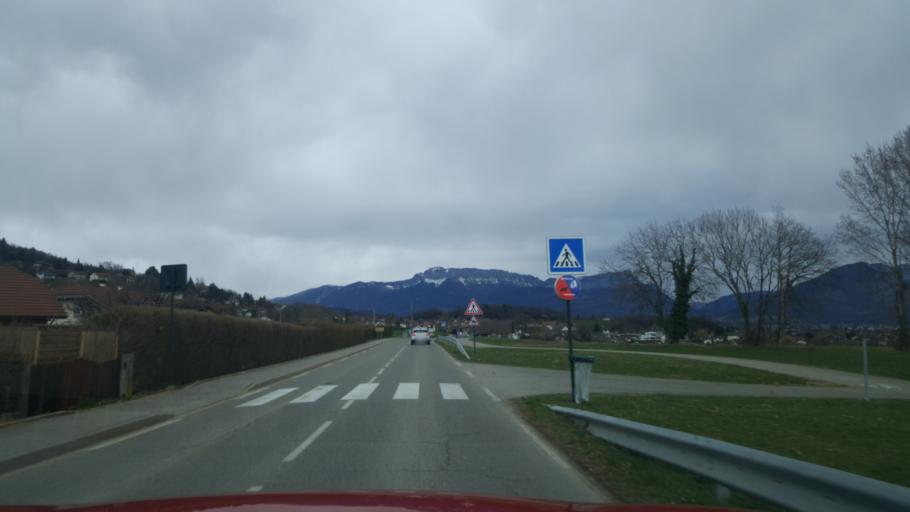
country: FR
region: Rhone-Alpes
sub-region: Departement de la Haute-Savoie
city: Epagny
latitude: 45.9448
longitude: 6.0755
